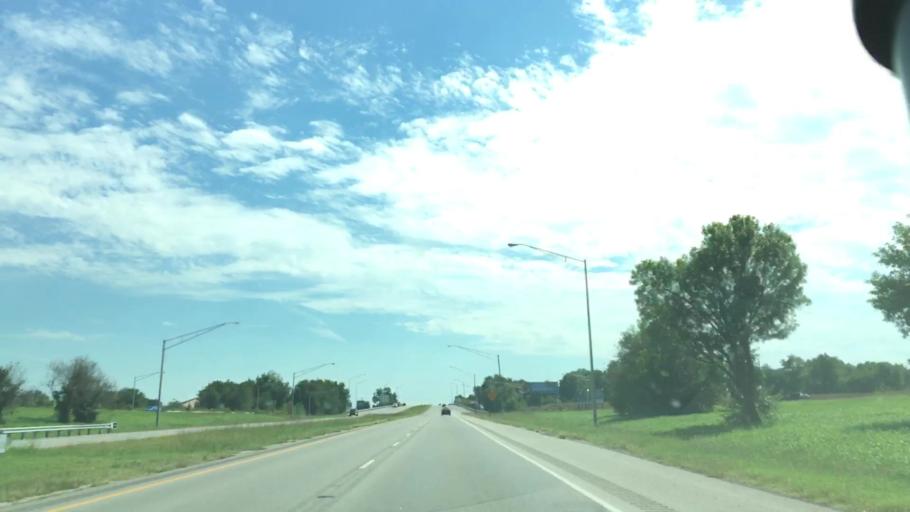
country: US
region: Kentucky
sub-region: Daviess County
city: Owensboro
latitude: 37.7549
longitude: -87.1587
